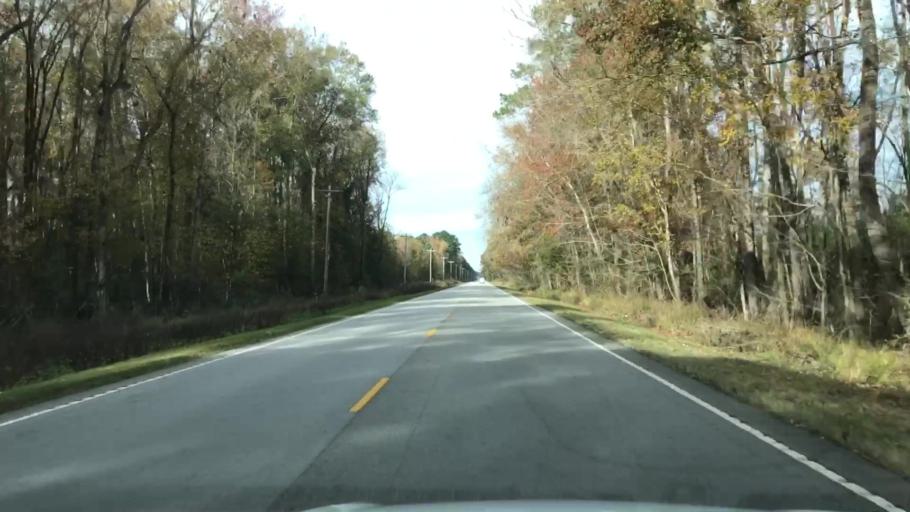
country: US
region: South Carolina
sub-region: Colleton County
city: Walterboro
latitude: 32.8106
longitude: -80.5263
